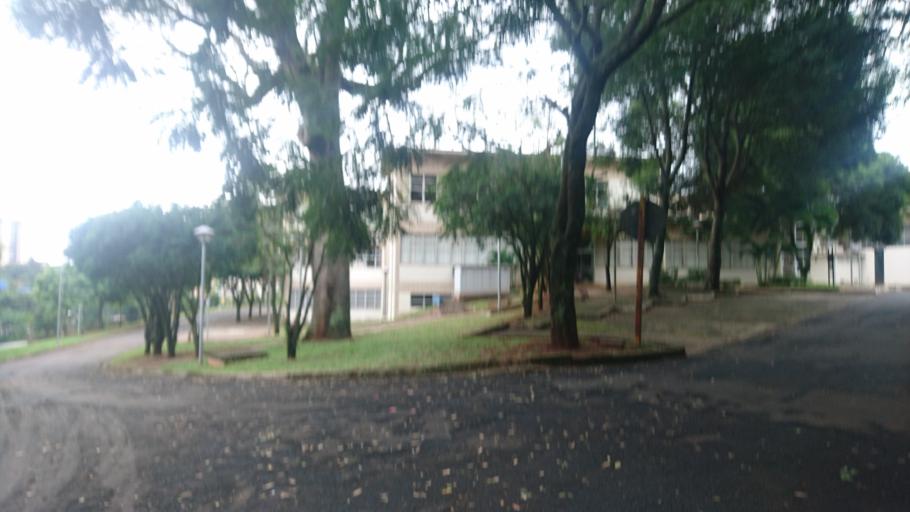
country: BR
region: Sao Paulo
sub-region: Sao Carlos
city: Sao Carlos
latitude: -22.0047
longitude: -47.8997
